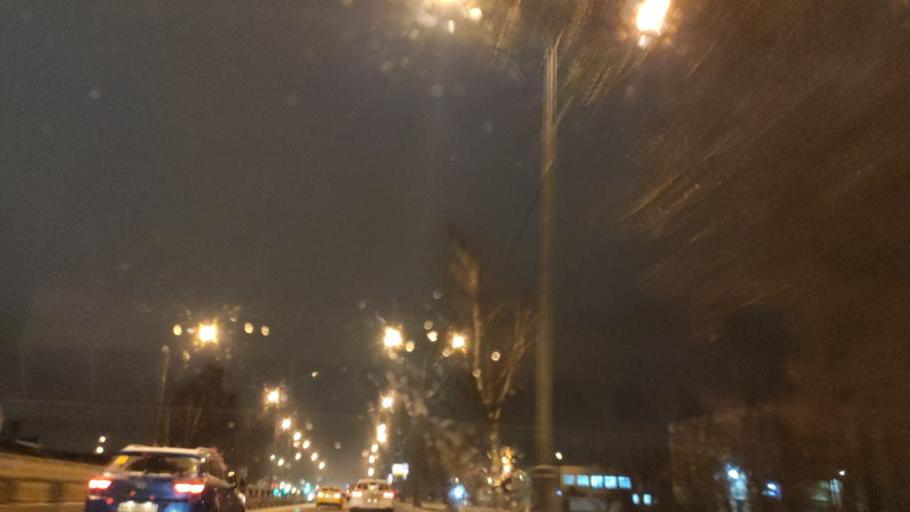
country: RU
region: Moskovskaya
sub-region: Leninskiy Rayon
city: Vnukovo
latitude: 55.6122
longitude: 37.2861
